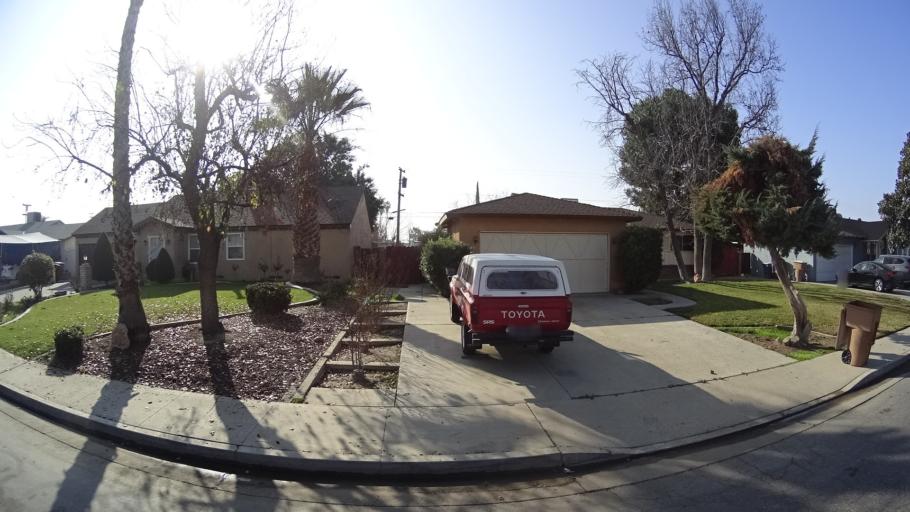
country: US
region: California
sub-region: Kern County
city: Bakersfield
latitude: 35.3304
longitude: -119.0265
